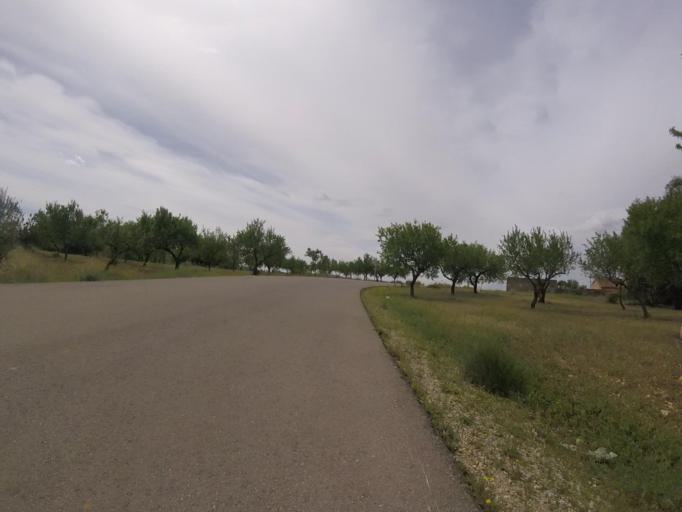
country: ES
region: Valencia
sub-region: Provincia de Castello
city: Benlloch
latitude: 40.1997
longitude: -0.0082
